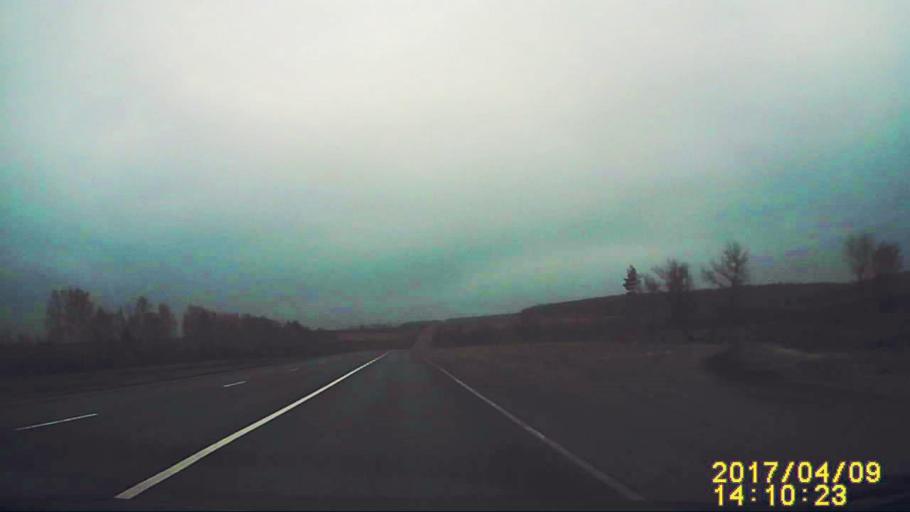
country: RU
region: Ulyanovsk
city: Krasnyy Gulyay
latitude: 54.0378
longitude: 48.2133
